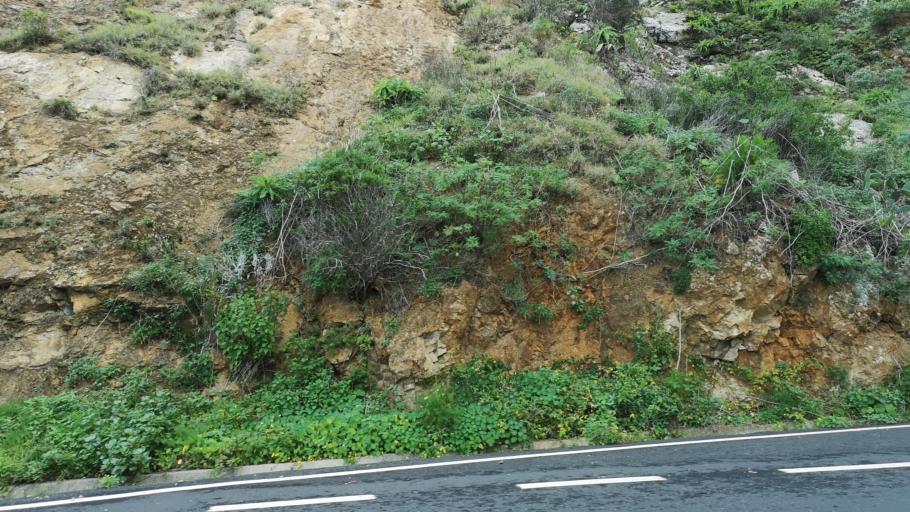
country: ES
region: Canary Islands
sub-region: Provincia de Santa Cruz de Tenerife
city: Agulo
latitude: 28.1886
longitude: -17.2073
